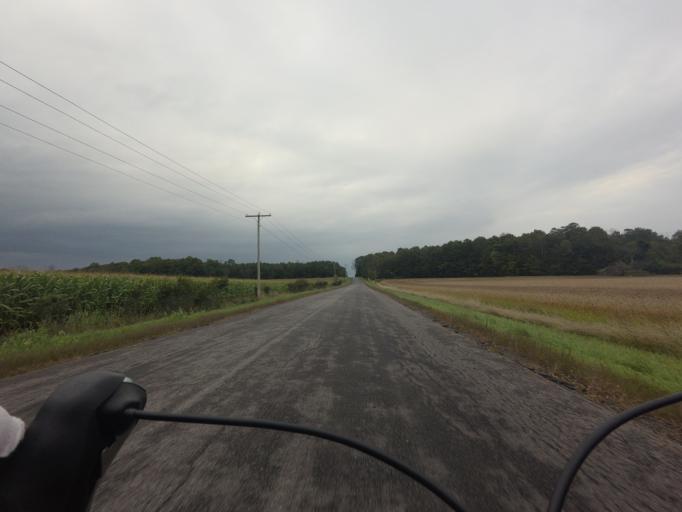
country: CA
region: Ontario
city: Bells Corners
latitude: 45.1495
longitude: -75.7521
